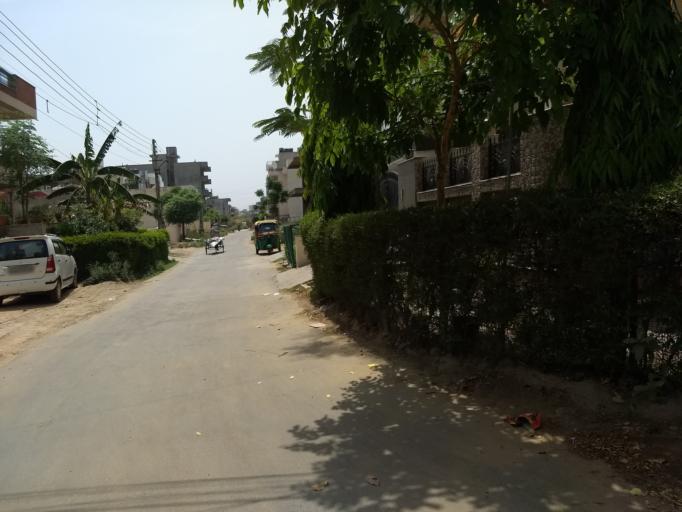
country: IN
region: Haryana
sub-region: Gurgaon
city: Gurgaon
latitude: 28.4543
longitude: 77.0949
